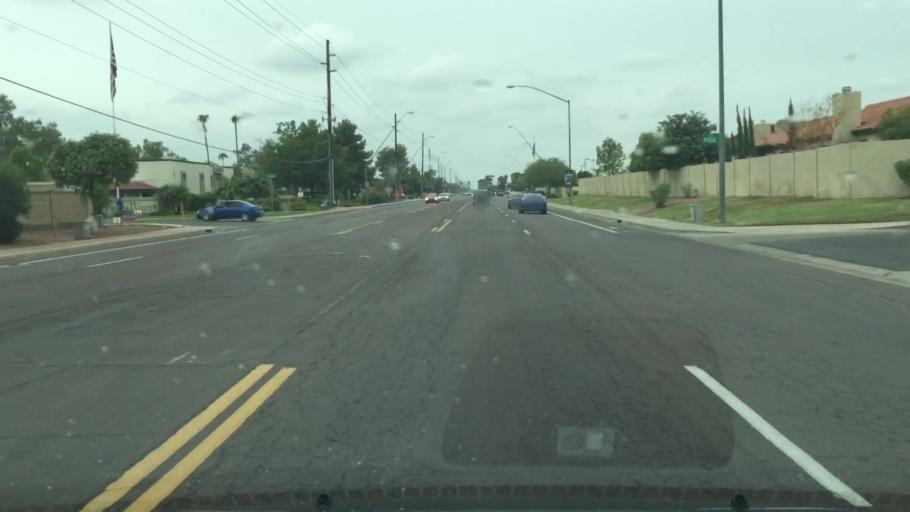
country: US
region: Arizona
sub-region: Maricopa County
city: Gilbert
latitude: 33.3936
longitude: -111.7835
